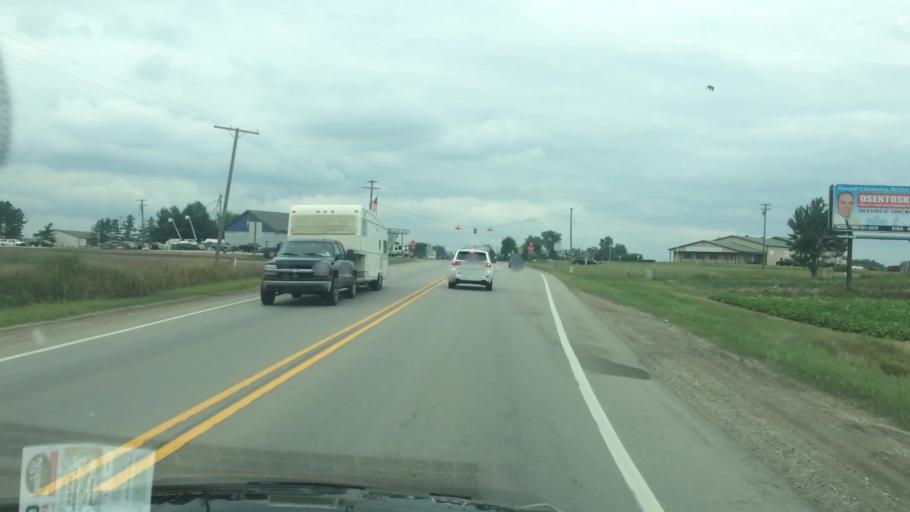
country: US
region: Michigan
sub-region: Sanilac County
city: Marlette
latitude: 43.4133
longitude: -83.0871
